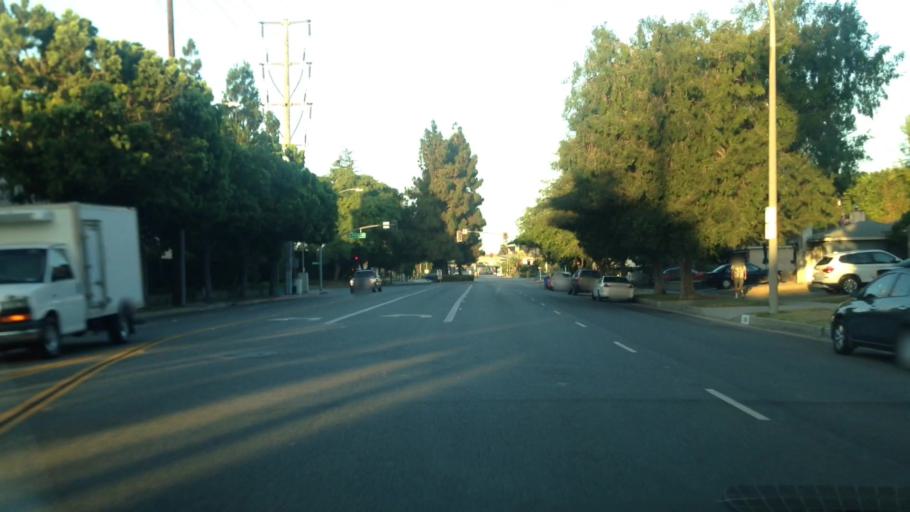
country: US
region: California
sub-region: Los Angeles County
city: Ladera Heights
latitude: 33.9916
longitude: -118.3931
